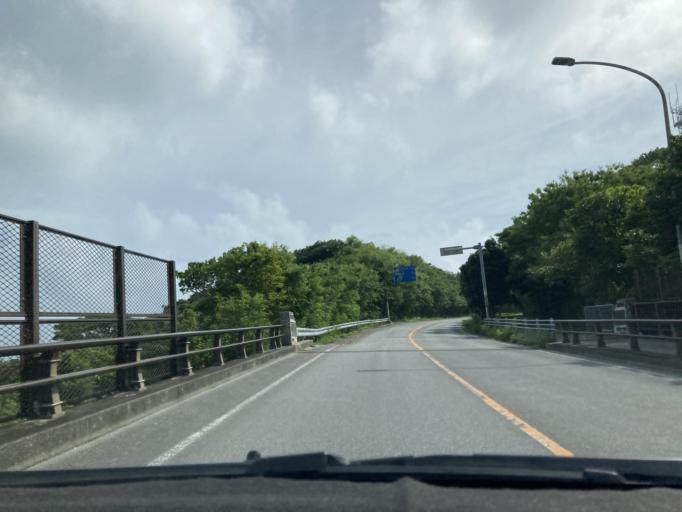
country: JP
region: Okinawa
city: Tomigusuku
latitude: 26.1444
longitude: 127.7953
